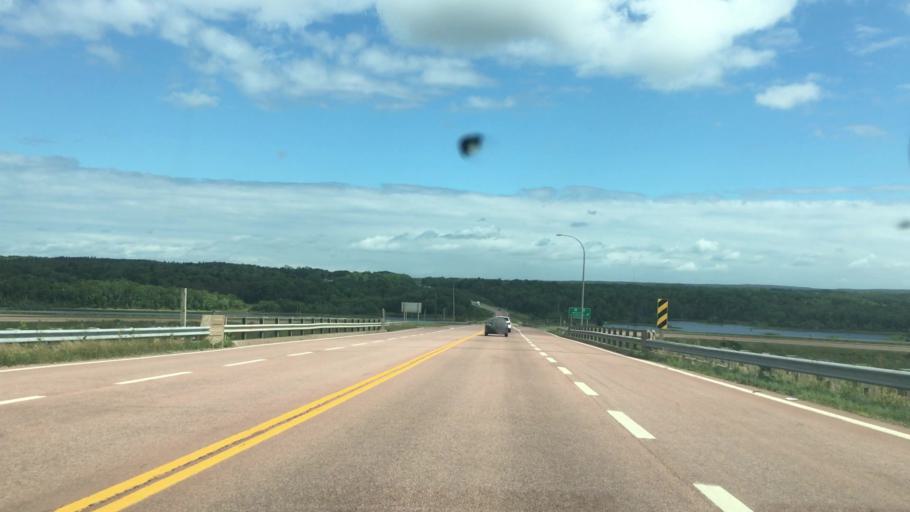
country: CA
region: Nova Scotia
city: Port Hawkesbury
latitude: 45.6138
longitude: -61.6284
